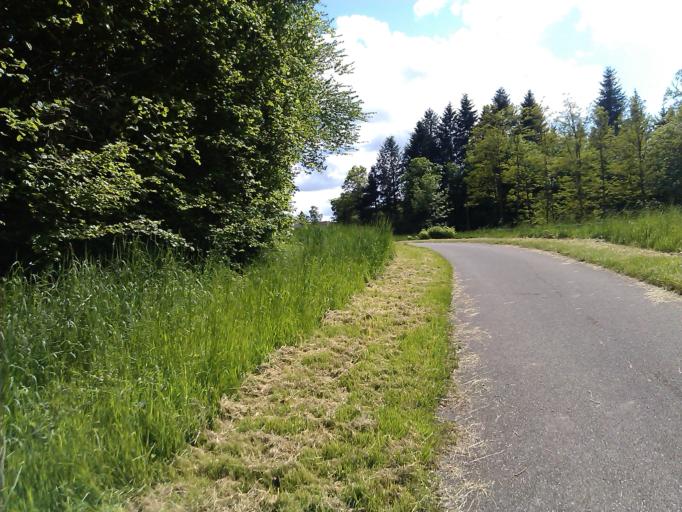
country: FR
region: Bourgogne
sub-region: Departement de Saone-et-Loire
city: Ecuisses
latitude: 46.7774
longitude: 4.5443
